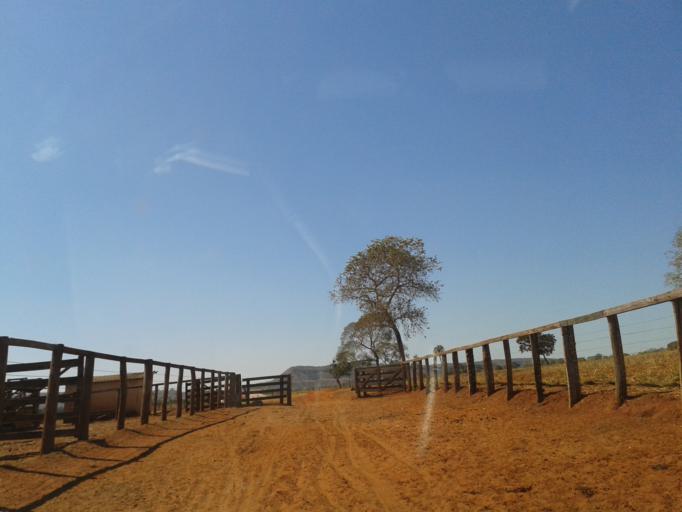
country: BR
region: Minas Gerais
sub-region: Santa Vitoria
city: Santa Vitoria
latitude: -19.0850
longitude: -50.0739
